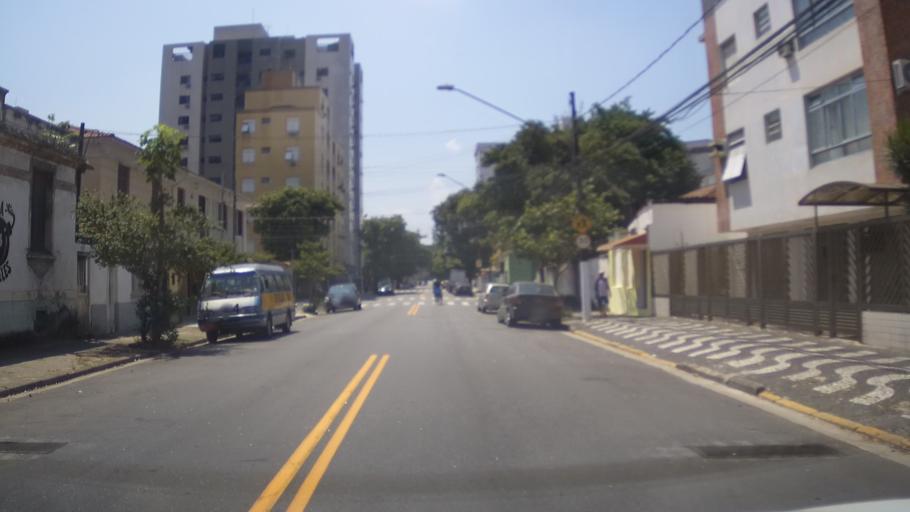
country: BR
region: Sao Paulo
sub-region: Santos
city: Santos
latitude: -23.9722
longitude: -46.3044
